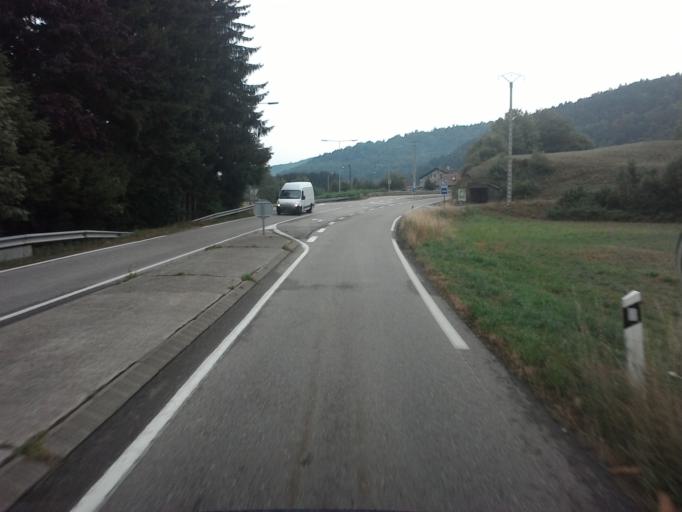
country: FR
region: Lorraine
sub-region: Departement des Vosges
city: Saint-Maurice-sur-Moselle
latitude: 47.8585
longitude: 6.8093
